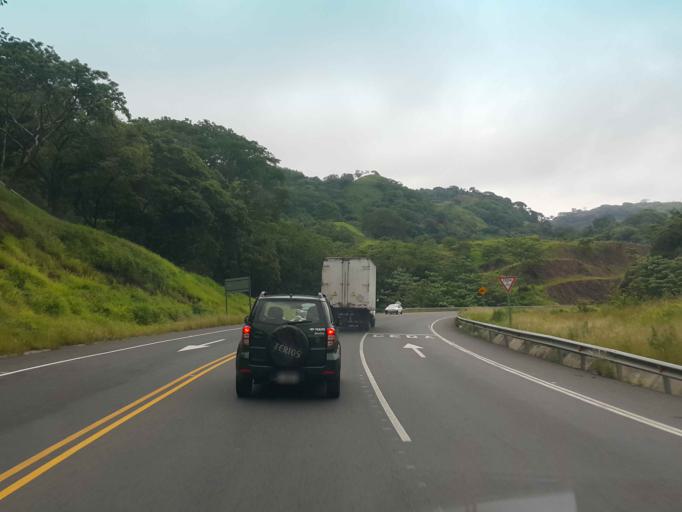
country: CR
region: Alajuela
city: Atenas
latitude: 9.9402
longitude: -84.4005
